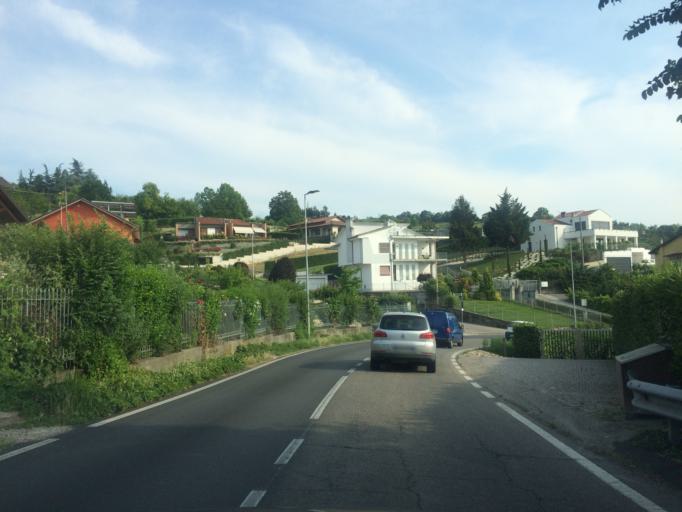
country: IT
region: Piedmont
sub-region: Provincia di Cuneo
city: Alba
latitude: 44.6990
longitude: 8.0456
